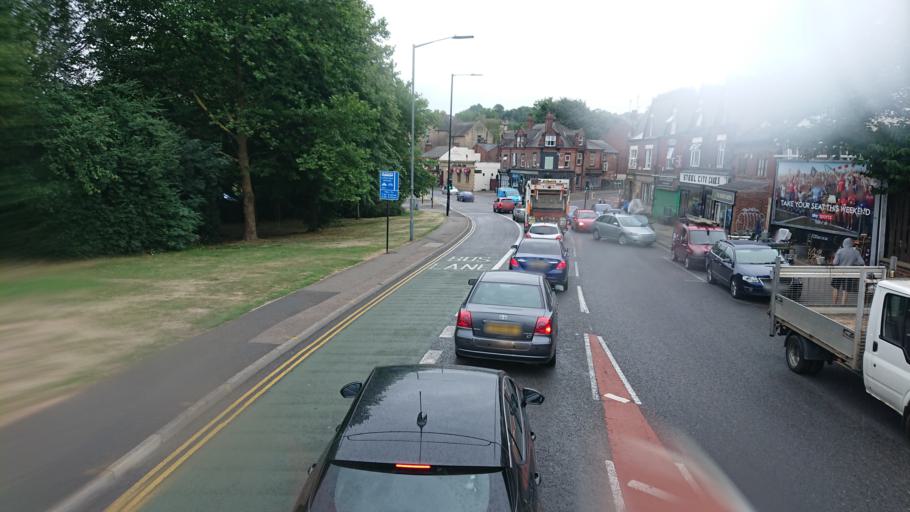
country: GB
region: England
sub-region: Sheffield
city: Sheffield
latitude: 53.3589
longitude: -1.4811
